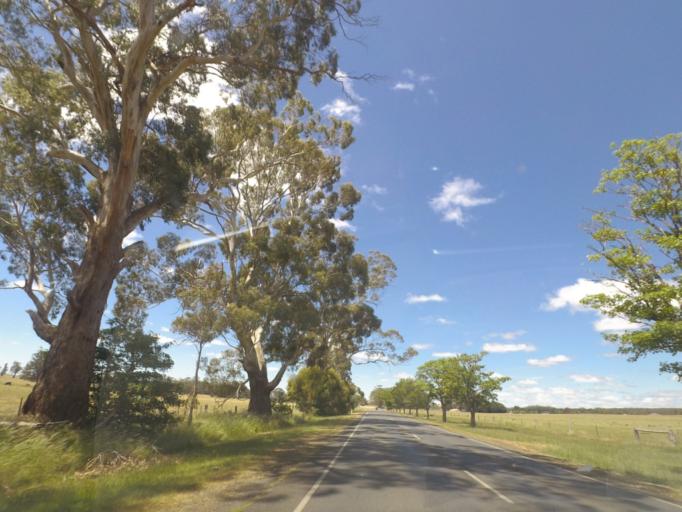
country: AU
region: Victoria
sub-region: Mount Alexander
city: Castlemaine
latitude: -37.3334
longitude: 144.1719
